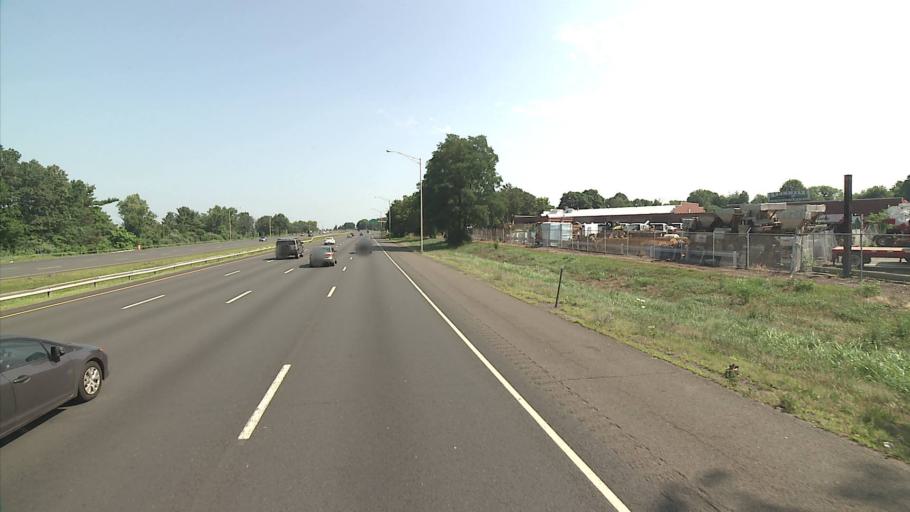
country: US
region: Connecticut
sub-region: New Haven County
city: North Haven
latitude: 41.3448
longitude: -72.8686
